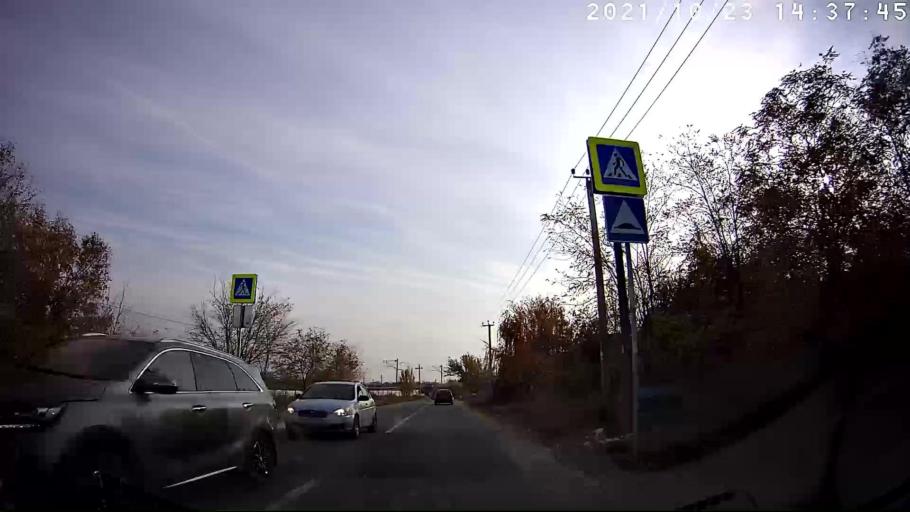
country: RU
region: Volgograd
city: Krasnoslobodsk
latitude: 48.4957
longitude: 44.5497
